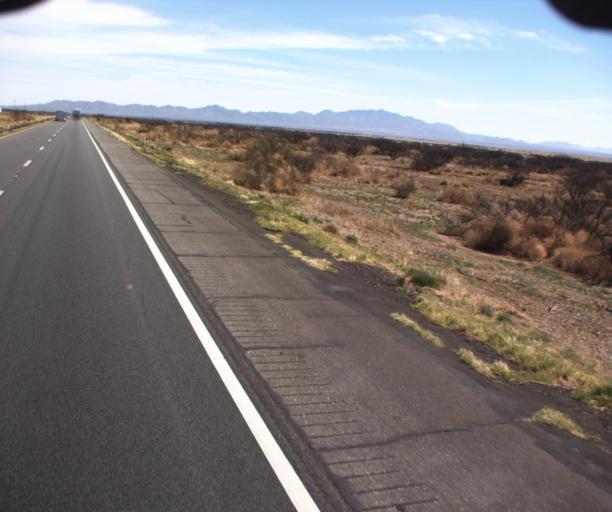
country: US
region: Arizona
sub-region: Cochise County
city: Willcox
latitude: 32.1860
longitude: -109.9331
